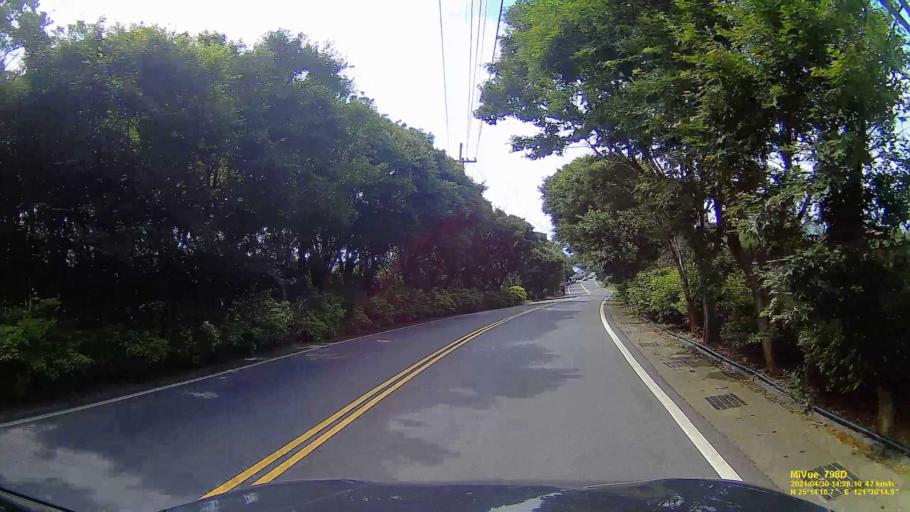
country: TW
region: Taipei
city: Taipei
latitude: 25.2387
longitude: 121.5038
